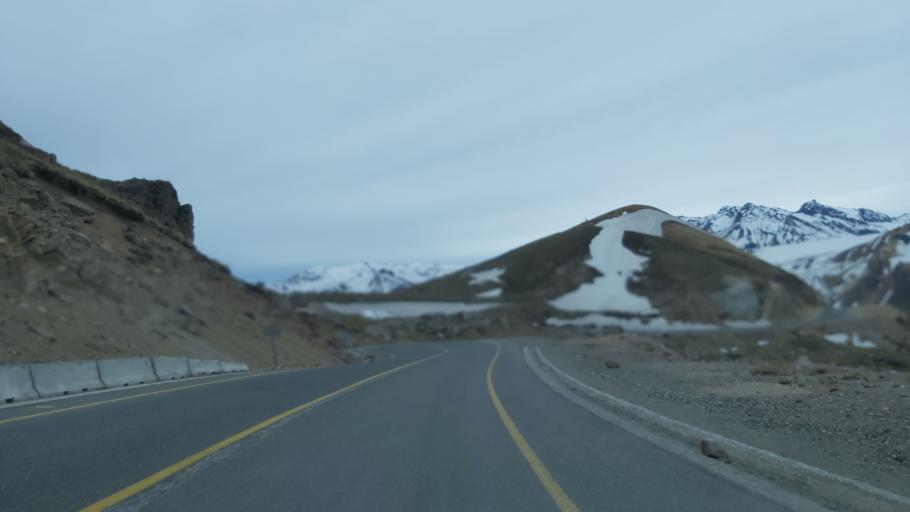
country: CL
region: Maule
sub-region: Provincia de Linares
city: Colbun
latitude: -35.9810
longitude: -70.5647
